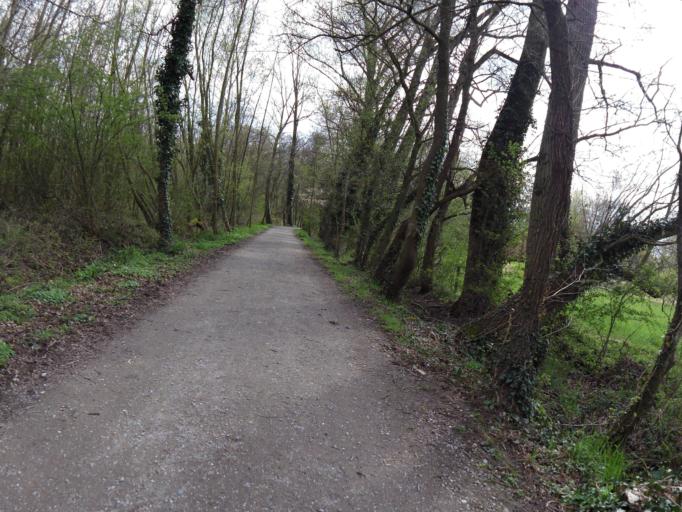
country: BE
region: Flanders
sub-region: Provincie Oost-Vlaanderen
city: Sint-Martens-Latem
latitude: 51.0278
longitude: 3.6289
